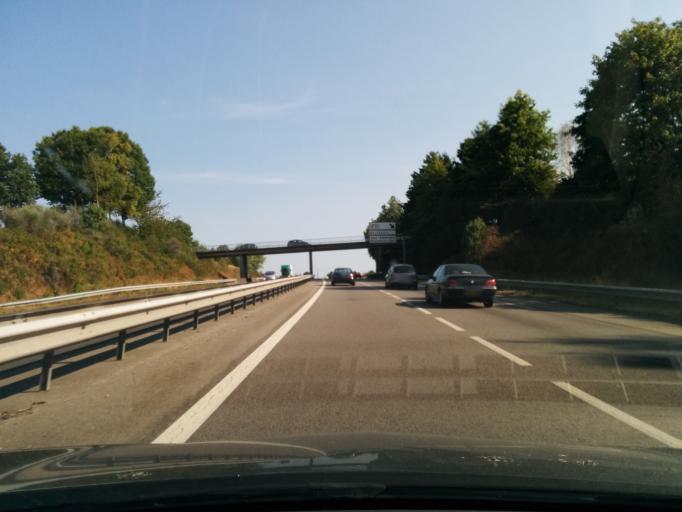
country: FR
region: Limousin
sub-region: Departement de la Haute-Vienne
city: Condat-sur-Vienne
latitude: 45.7826
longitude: 1.3035
